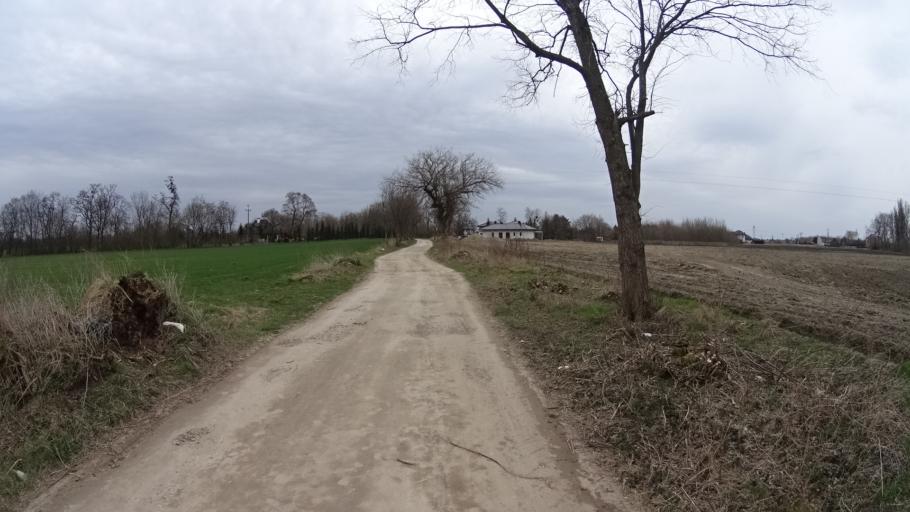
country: PL
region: Masovian Voivodeship
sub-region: Powiat warszawski zachodni
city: Ozarow Mazowiecki
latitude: 52.2333
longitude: 20.7885
